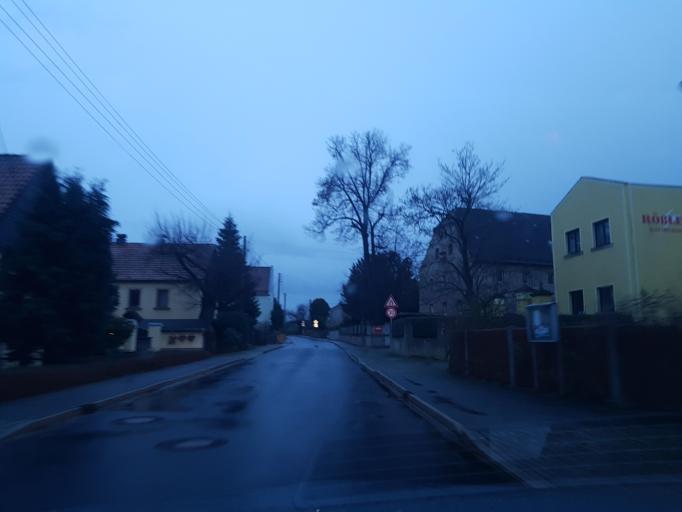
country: DE
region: Saxony
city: Priestewitz
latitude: 51.2432
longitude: 13.5192
